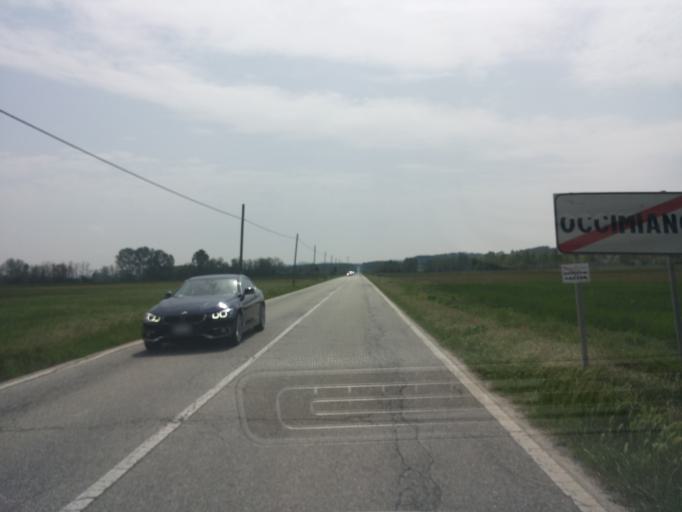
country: IT
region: Piedmont
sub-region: Provincia di Alessandria
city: Occimiano
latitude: 45.0540
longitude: 8.5136
